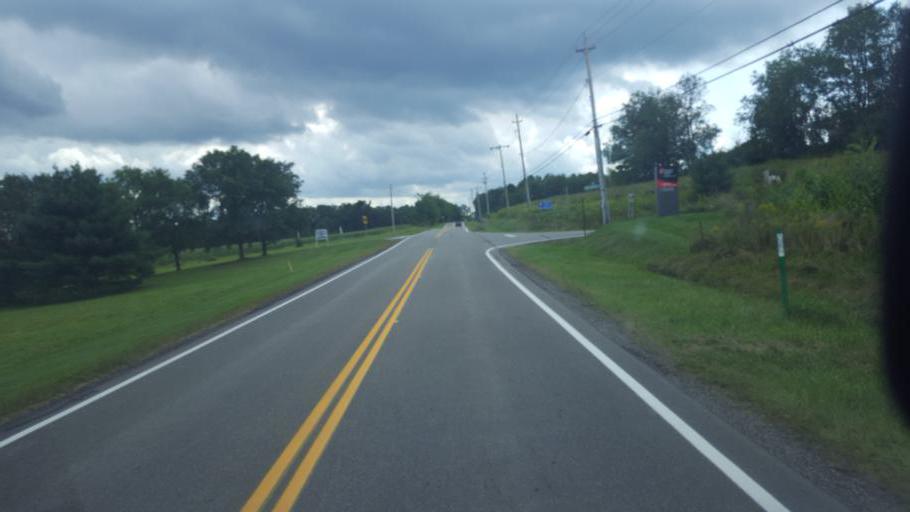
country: US
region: Ohio
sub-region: Geauga County
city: Burton
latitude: 41.5095
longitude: -81.1807
